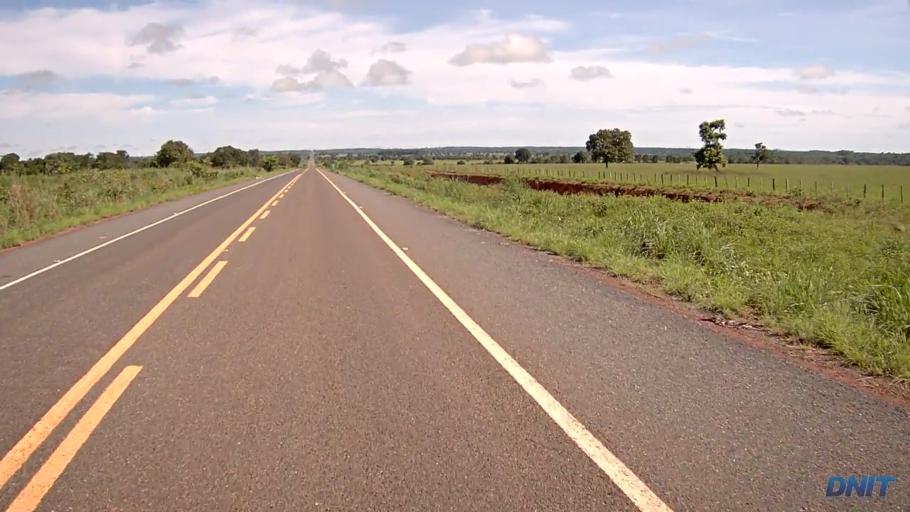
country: BR
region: Goias
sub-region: Sao Miguel Do Araguaia
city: Sao Miguel do Araguaia
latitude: -13.4093
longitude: -50.1326
